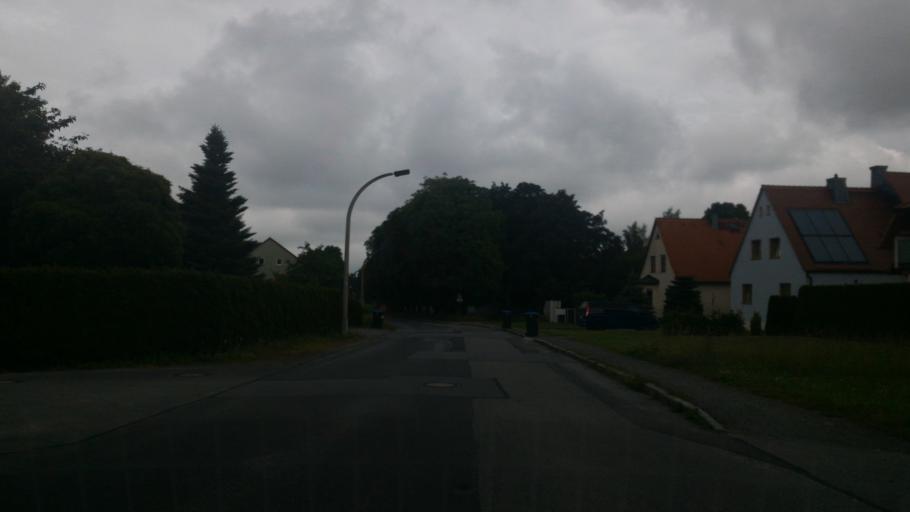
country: DE
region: Saxony
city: Neugersdorf
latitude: 50.9817
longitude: 14.6209
